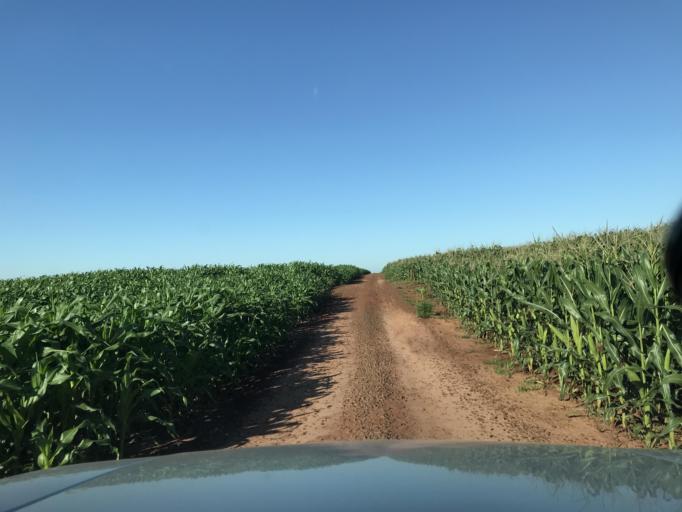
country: BR
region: Parana
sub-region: Palotina
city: Palotina
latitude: -24.2303
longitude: -53.7625
